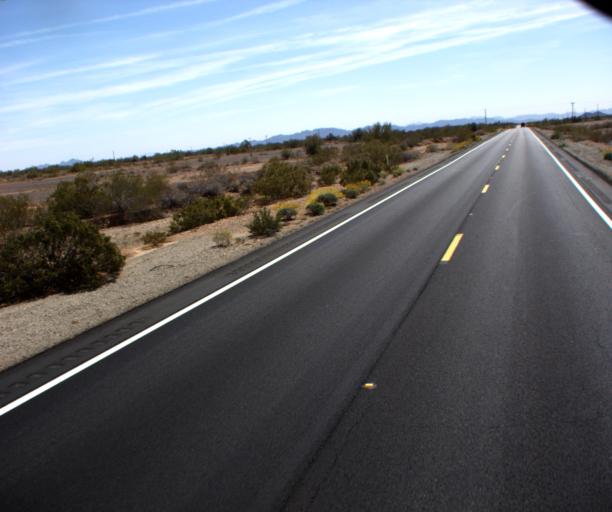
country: US
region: Arizona
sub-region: Yuma County
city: Wellton
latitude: 32.9981
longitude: -114.2863
